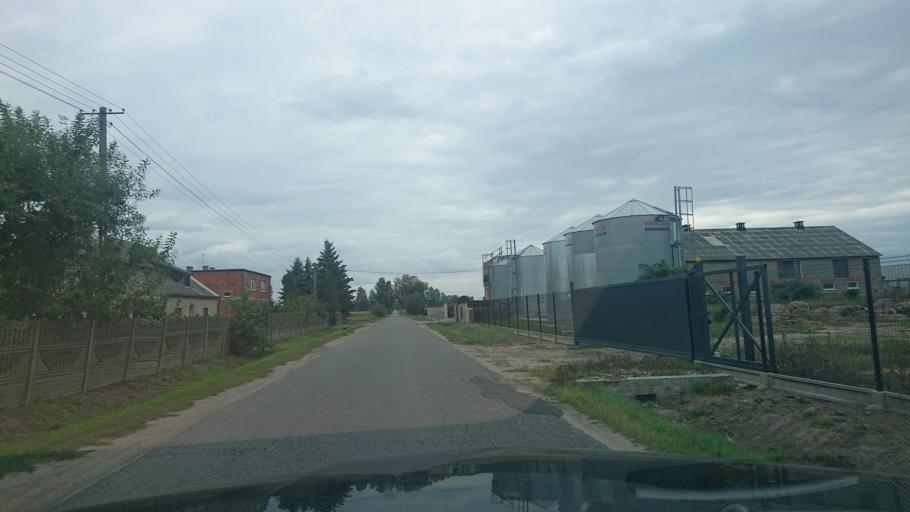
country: PL
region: Greater Poland Voivodeship
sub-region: Powiat gnieznienski
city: Niechanowo
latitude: 52.4672
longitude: 17.6214
